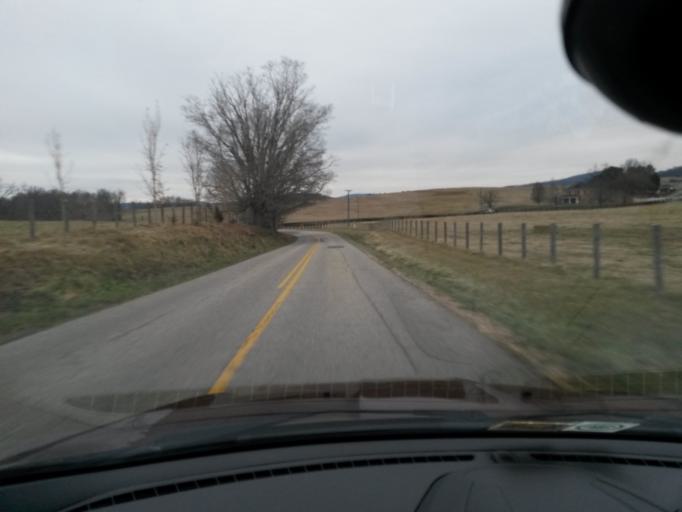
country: US
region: Virginia
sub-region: Rockbridge County
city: East Lexington
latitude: 37.9163
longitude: -79.3185
